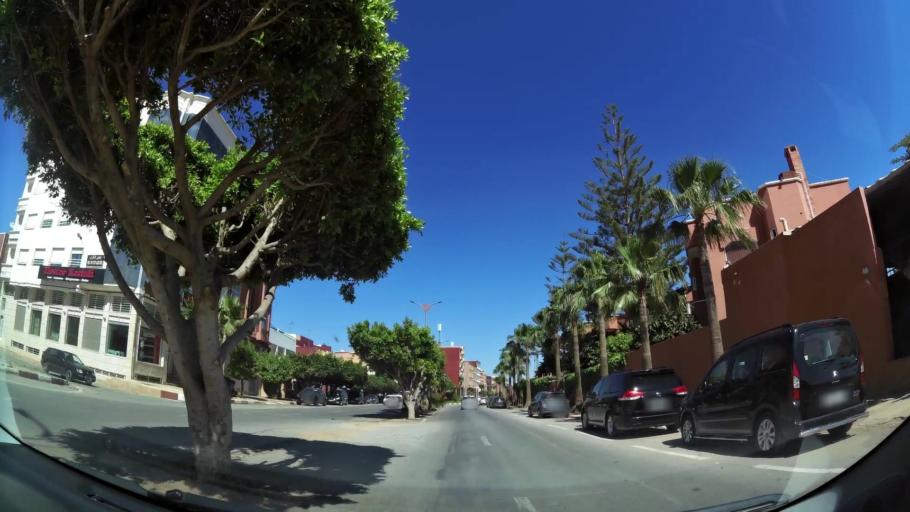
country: MA
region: Oriental
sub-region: Berkane-Taourirt
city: Berkane
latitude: 34.9344
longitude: -2.3260
